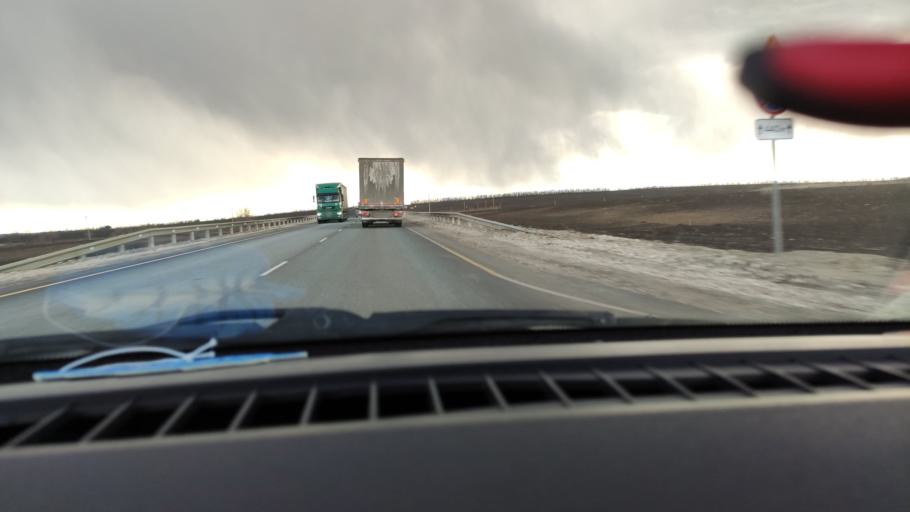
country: RU
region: Saratov
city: Yelshanka
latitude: 51.8433
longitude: 46.4805
